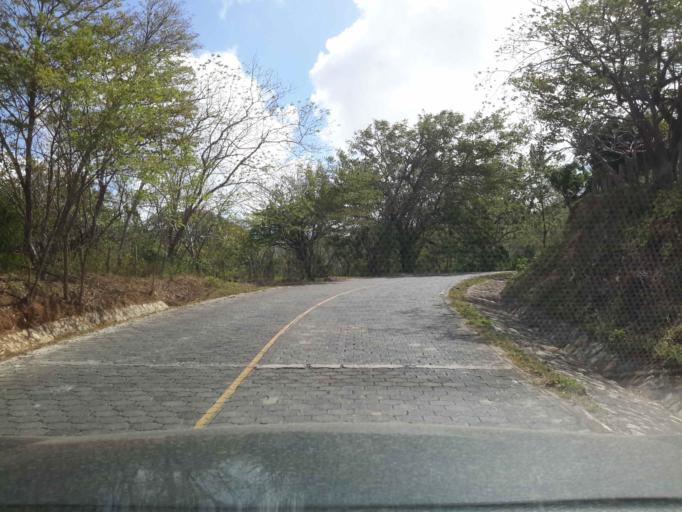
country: NI
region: Rivas
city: San Juan del Sur
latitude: 11.2261
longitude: -85.8187
